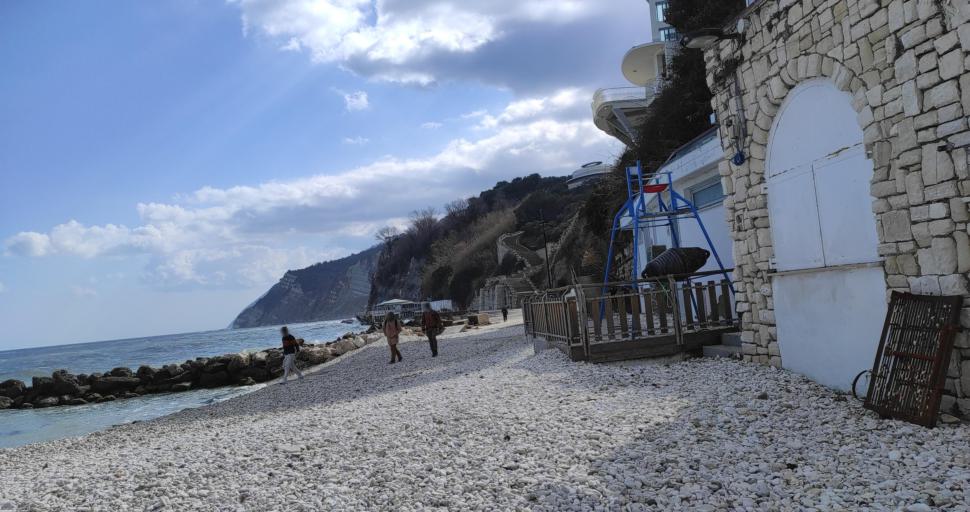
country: IT
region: The Marches
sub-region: Provincia di Ancona
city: Pietra la Croce
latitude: 43.6168
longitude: 13.5337
